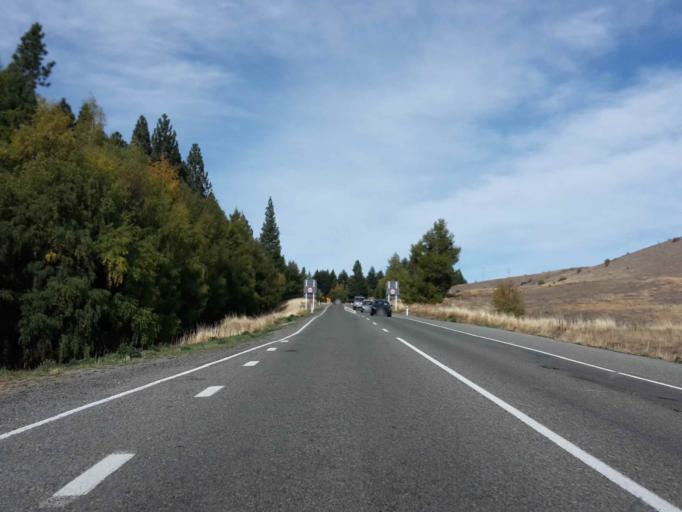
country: NZ
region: Canterbury
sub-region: Timaru District
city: Pleasant Point
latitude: -44.0087
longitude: 170.4956
